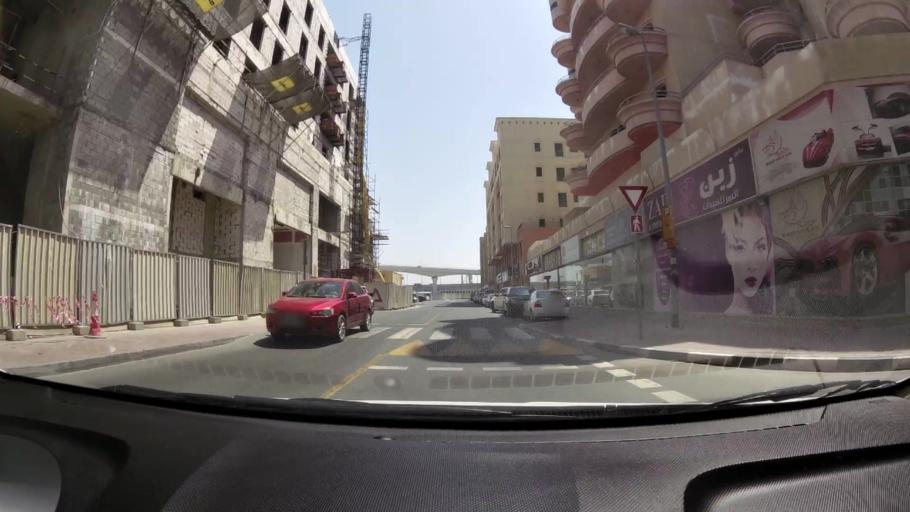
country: AE
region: Ash Shariqah
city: Sharjah
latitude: 25.2775
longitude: 55.3503
